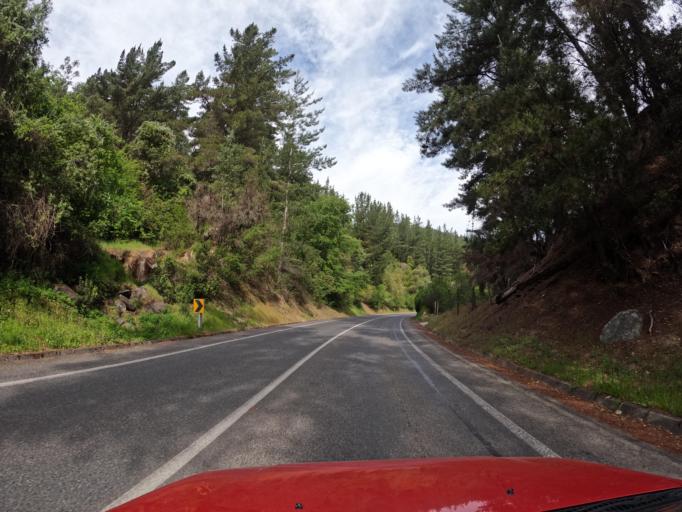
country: CL
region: Maule
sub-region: Provincia de Talca
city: Talca
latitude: -35.2974
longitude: -71.9632
